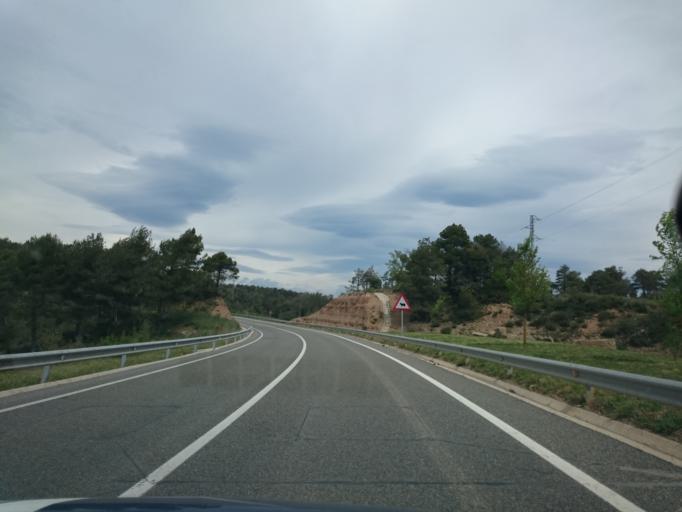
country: ES
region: Catalonia
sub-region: Provincia de Barcelona
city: Olost
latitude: 41.9437
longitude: 2.1407
